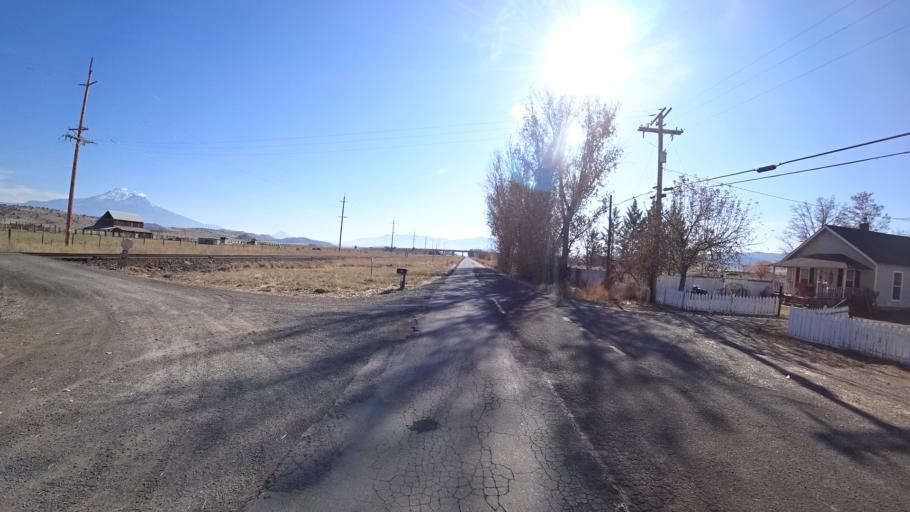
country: US
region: California
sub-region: Siskiyou County
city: Montague
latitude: 41.6325
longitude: -122.5219
